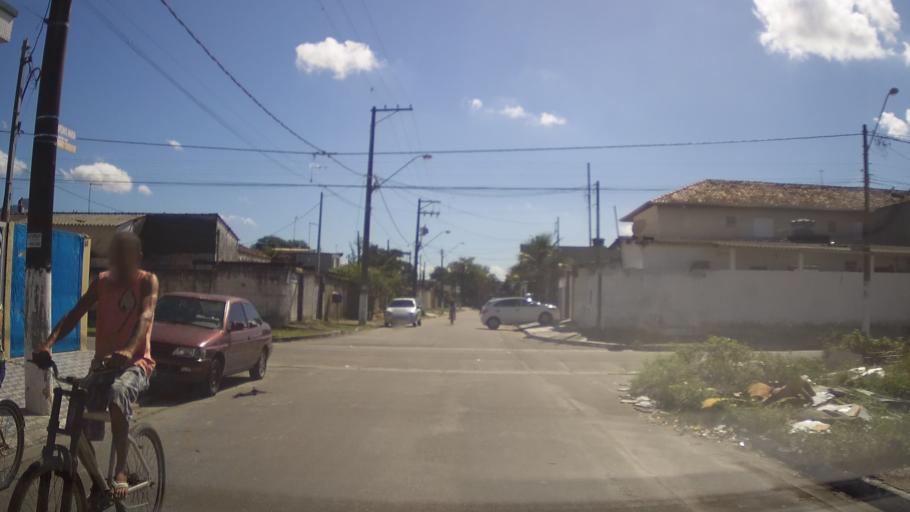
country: BR
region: Sao Paulo
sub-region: Mongagua
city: Mongagua
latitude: -24.0258
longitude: -46.5318
